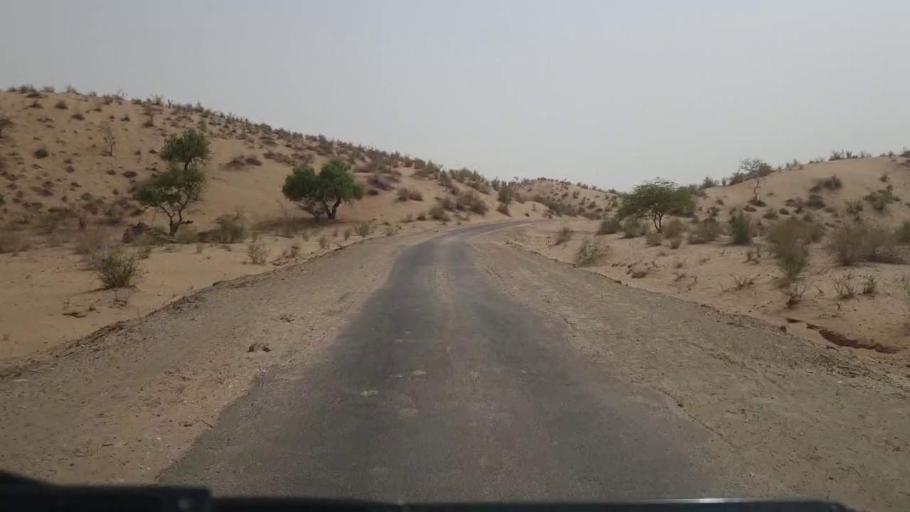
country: PK
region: Sindh
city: Islamkot
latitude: 25.2611
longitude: 70.6462
